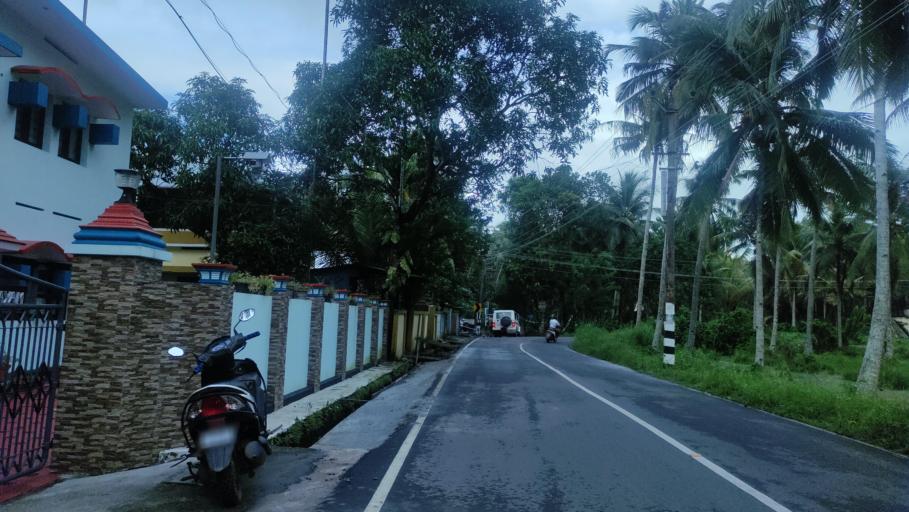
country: IN
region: Kerala
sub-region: Alappuzha
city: Kayankulam
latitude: 9.1949
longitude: 76.5038
